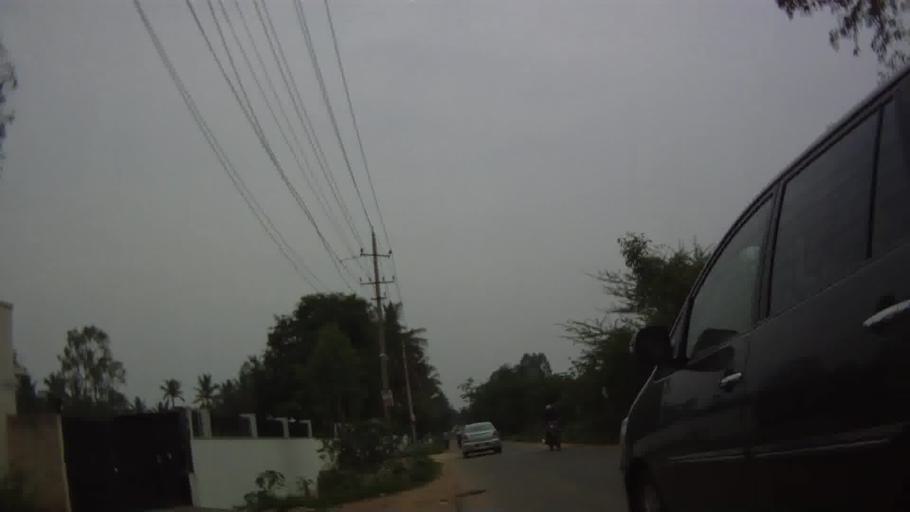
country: IN
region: Karnataka
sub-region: Bangalore Urban
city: Bangalore
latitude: 12.9652
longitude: 77.7037
